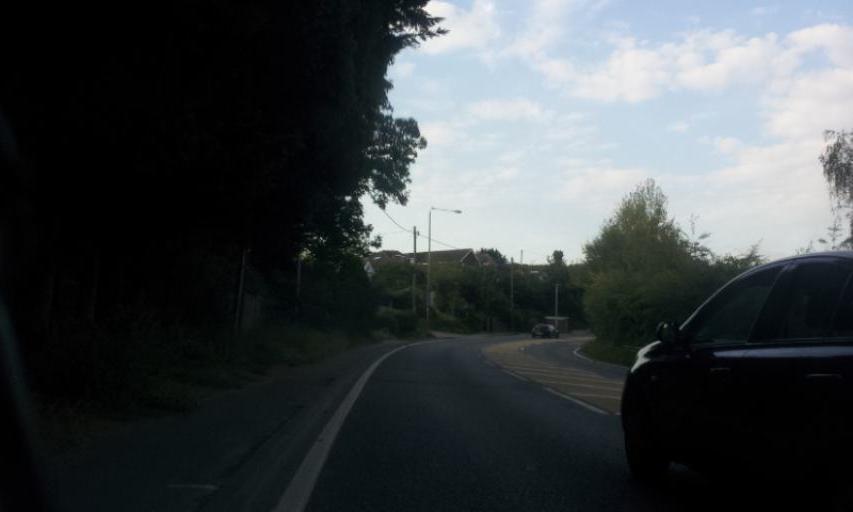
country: GB
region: England
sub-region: Medway
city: Cuxton
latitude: 51.3747
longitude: 0.4579
